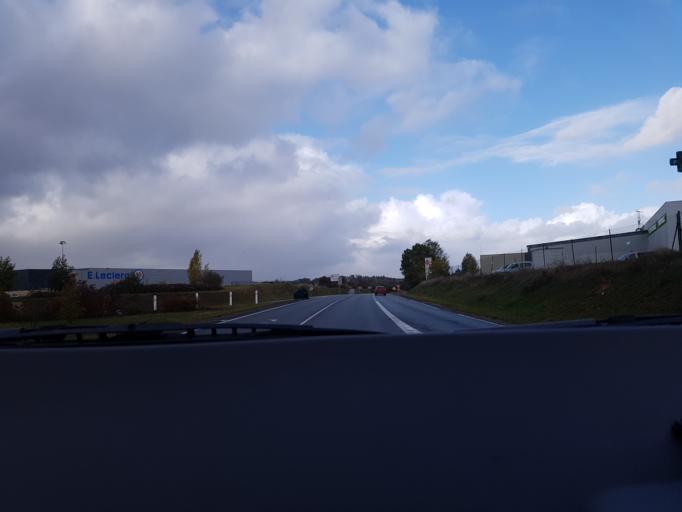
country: FR
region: Poitou-Charentes
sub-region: Departement de la Charente-Maritime
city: Pons
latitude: 45.5739
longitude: -0.5582
